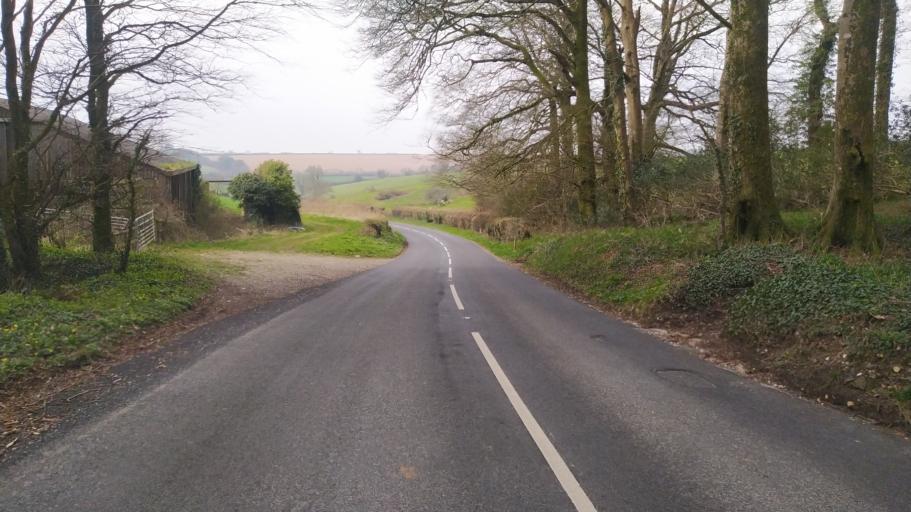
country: GB
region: England
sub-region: Dorset
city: Beaminster
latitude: 50.8203
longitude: -2.6830
